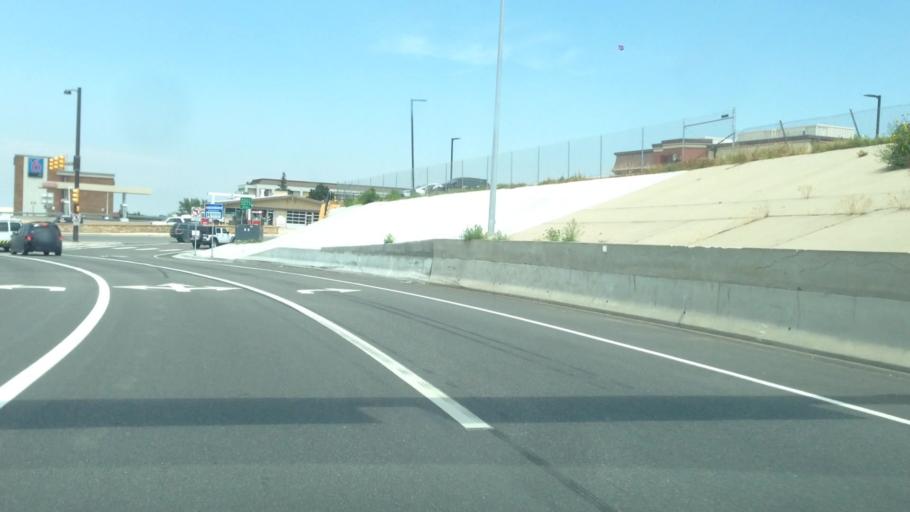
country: US
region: Colorado
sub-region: Arapahoe County
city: Centennial
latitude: 39.5939
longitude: -104.8828
